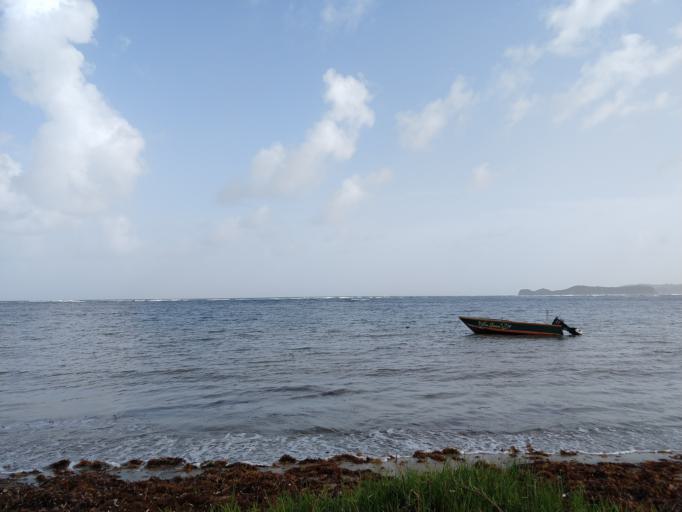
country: GD
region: Saint Andrew
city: Grenville
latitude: 12.1248
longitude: -61.6163
